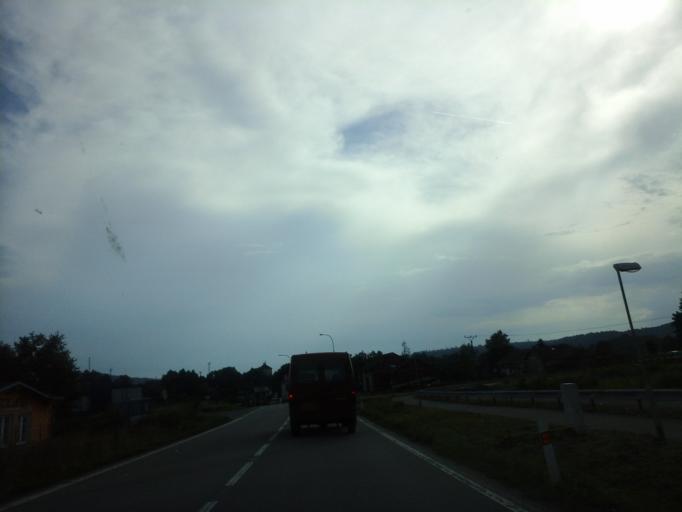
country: CZ
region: Pardubicky
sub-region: Okres Usti nad Orlici
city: Lanskroun
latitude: 49.8960
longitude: 16.5789
